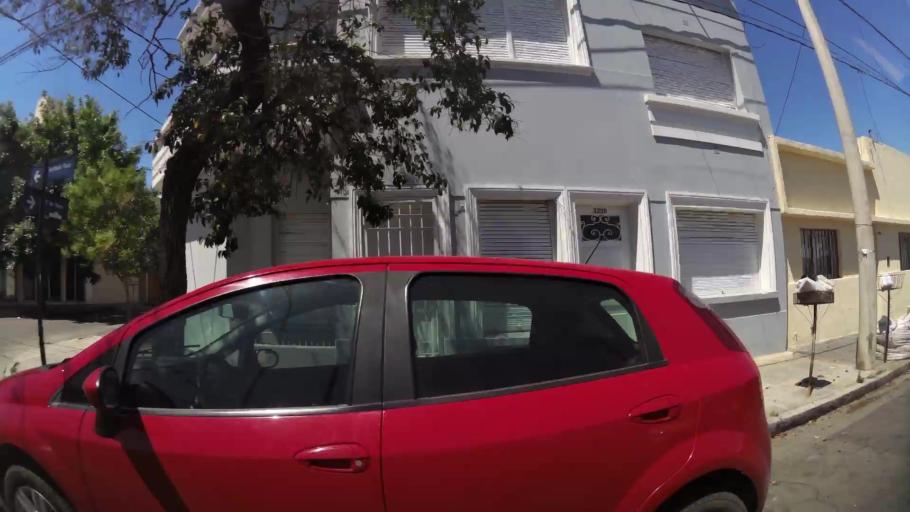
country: AR
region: Cordoba
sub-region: Departamento de Capital
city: Cordoba
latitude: -31.3823
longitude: -64.2020
